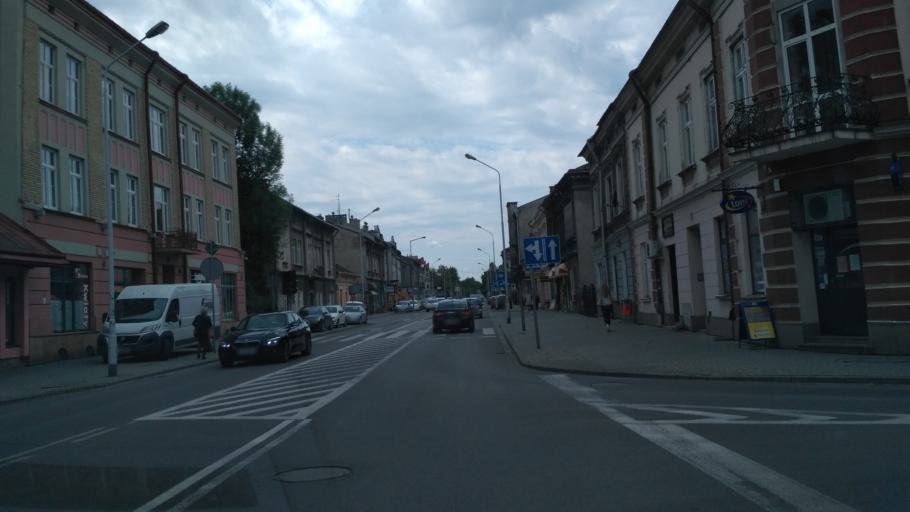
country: PL
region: Subcarpathian Voivodeship
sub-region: Przemysl
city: Przemysl
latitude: 49.7862
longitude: 22.7618
